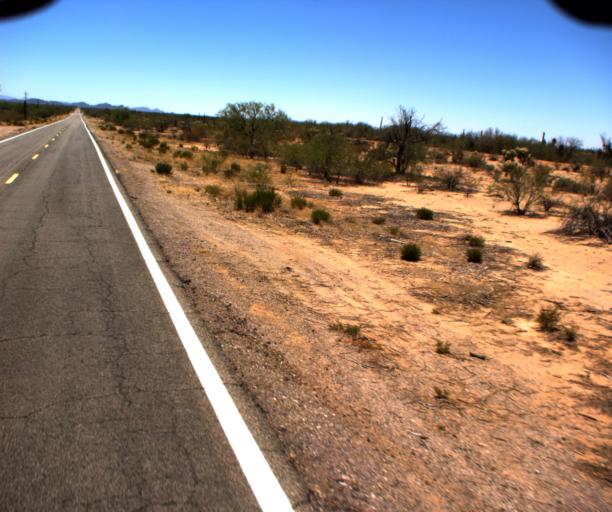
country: US
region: Arizona
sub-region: Pima County
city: Sells
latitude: 32.0954
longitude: -112.0618
